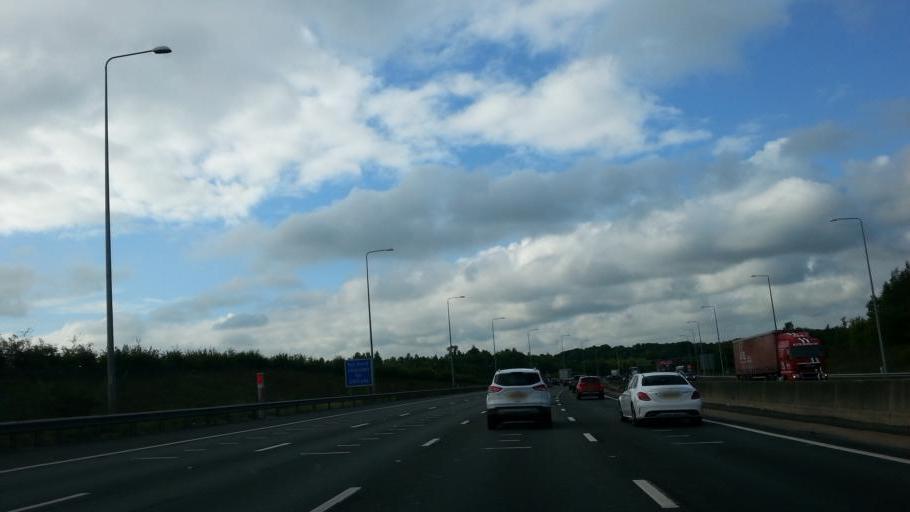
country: GB
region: England
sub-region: Hertfordshire
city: Kings Langley
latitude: 51.6834
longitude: -0.4487
